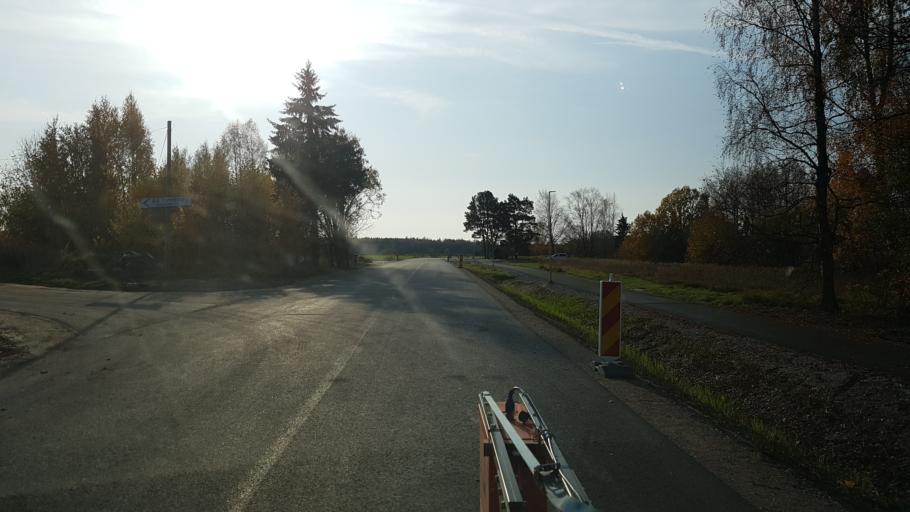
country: EE
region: Paernumaa
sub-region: Paikuse vald
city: Paikuse
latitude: 58.3419
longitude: 24.6198
